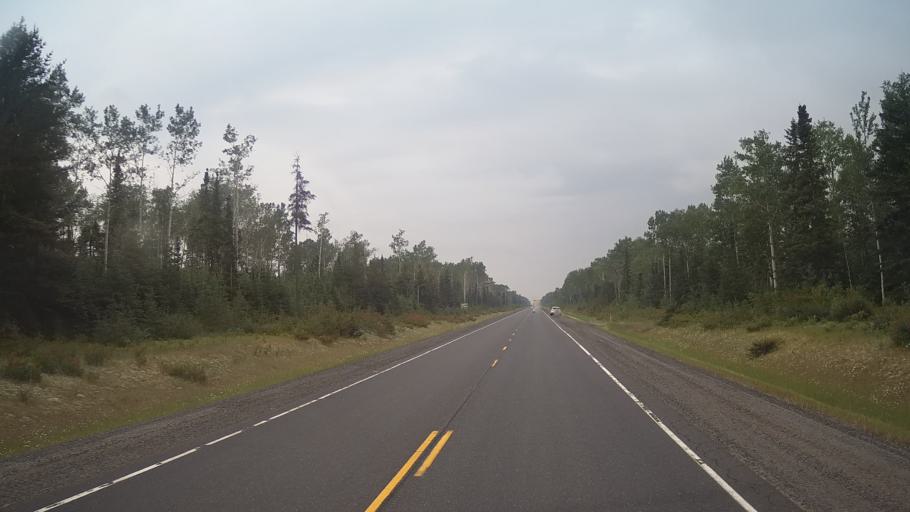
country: CA
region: Ontario
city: Greenstone
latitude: 49.2336
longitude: -88.1832
